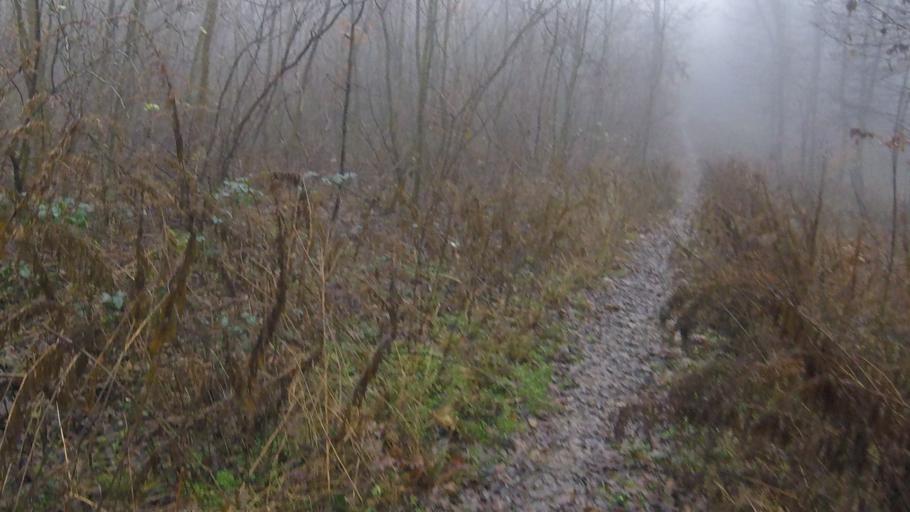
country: HU
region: Pest
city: Biatorbagy
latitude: 47.4575
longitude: 18.8522
